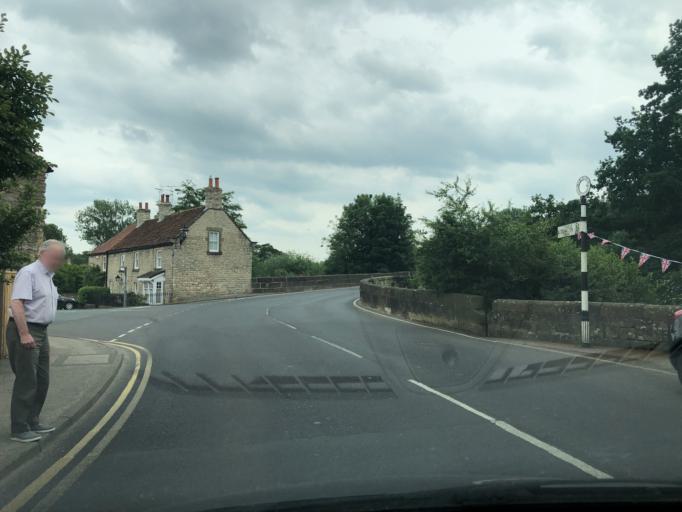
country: GB
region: England
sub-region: North Yorkshire
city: Helmsley
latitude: 54.2447
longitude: -1.0597
